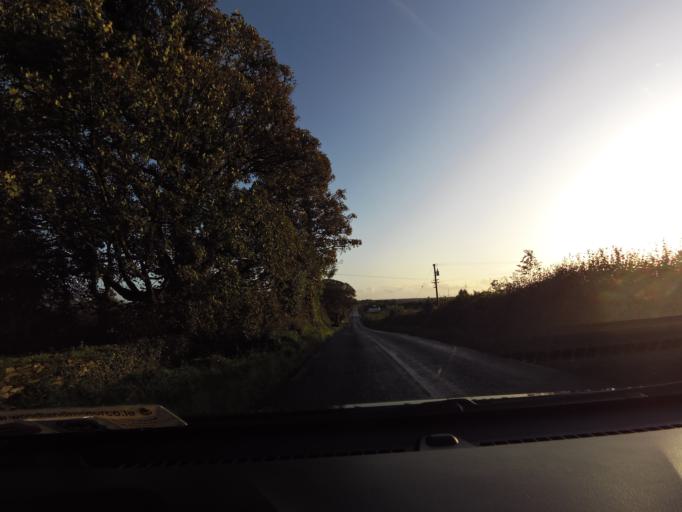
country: IE
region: Connaught
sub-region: Roscommon
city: Castlerea
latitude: 53.7365
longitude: -8.5506
